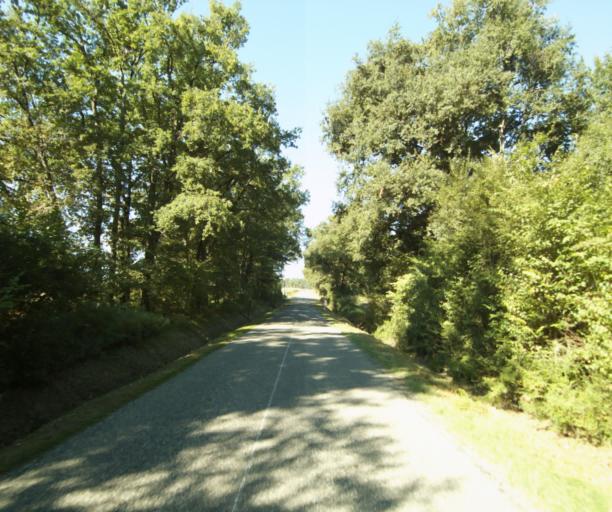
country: FR
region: Aquitaine
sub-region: Departement des Landes
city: Gabarret
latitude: 43.9526
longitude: -0.0078
